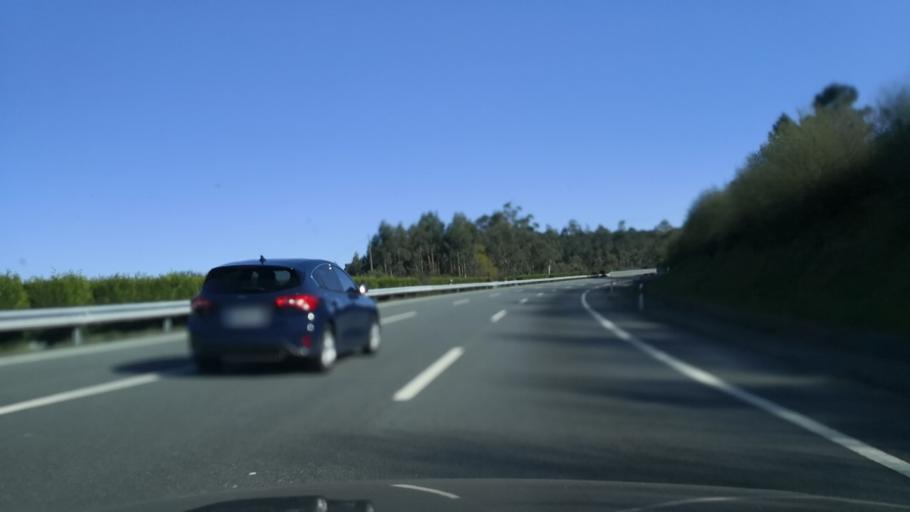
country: ES
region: Galicia
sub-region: Provincia da Coruna
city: Aranga
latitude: 43.2314
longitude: -8.0658
